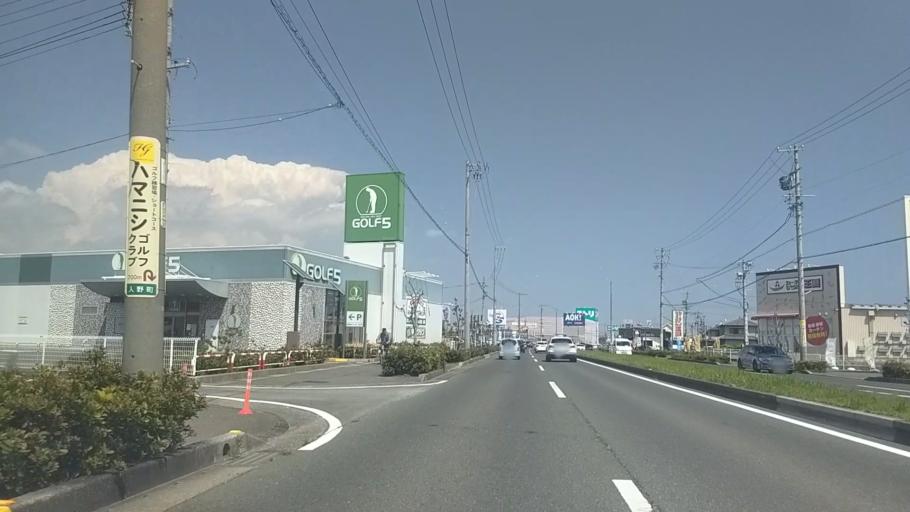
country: JP
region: Shizuoka
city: Hamamatsu
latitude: 34.6990
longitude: 137.6699
